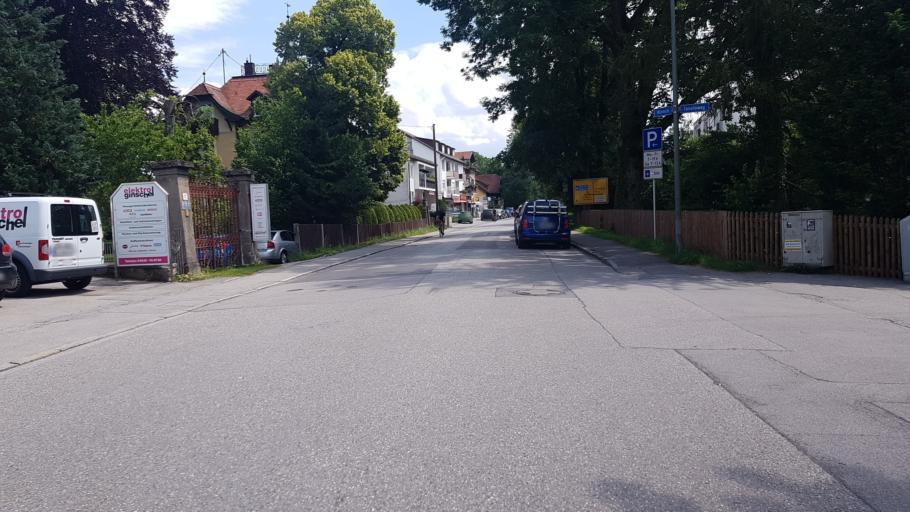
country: DE
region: Bavaria
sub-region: Upper Bavaria
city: Starnberg
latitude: 48.0000
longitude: 11.3608
